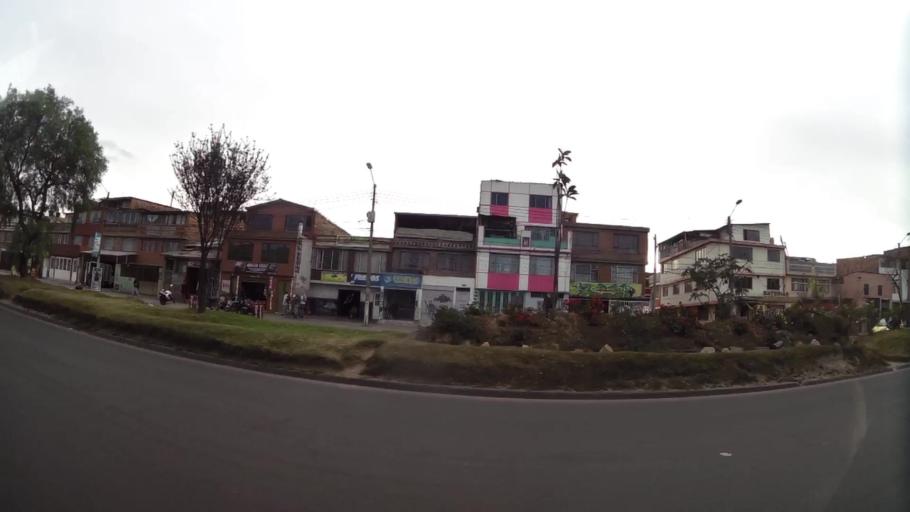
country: CO
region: Cundinamarca
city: Soacha
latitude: 4.6168
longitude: -74.1634
